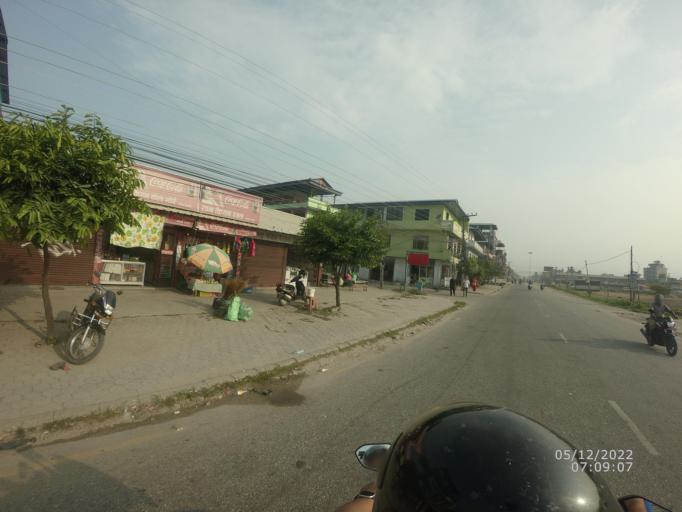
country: NP
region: Central Region
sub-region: Narayani Zone
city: Bharatpur
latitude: 27.6691
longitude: 84.4383
